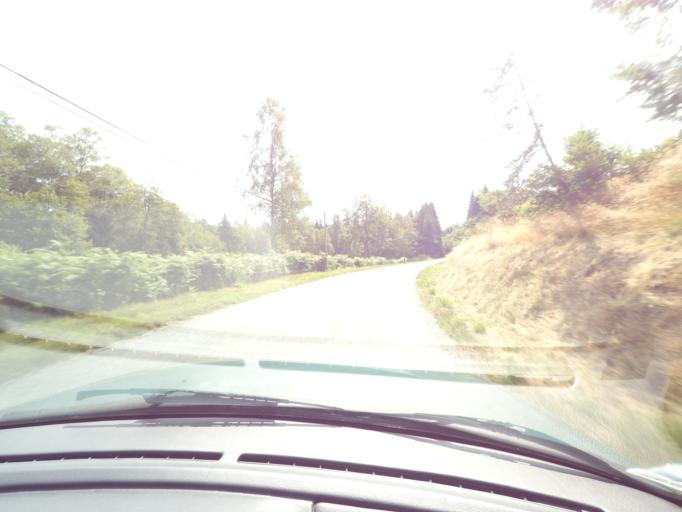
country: FR
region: Limousin
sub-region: Departement de la Correze
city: Bugeat
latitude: 45.7528
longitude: 1.9554
